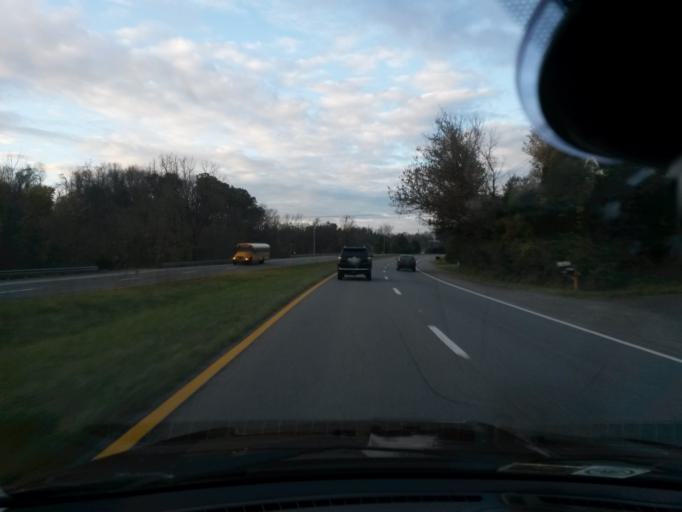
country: US
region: Virginia
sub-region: Botetourt County
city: Fincastle
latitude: 37.4599
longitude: -79.8842
